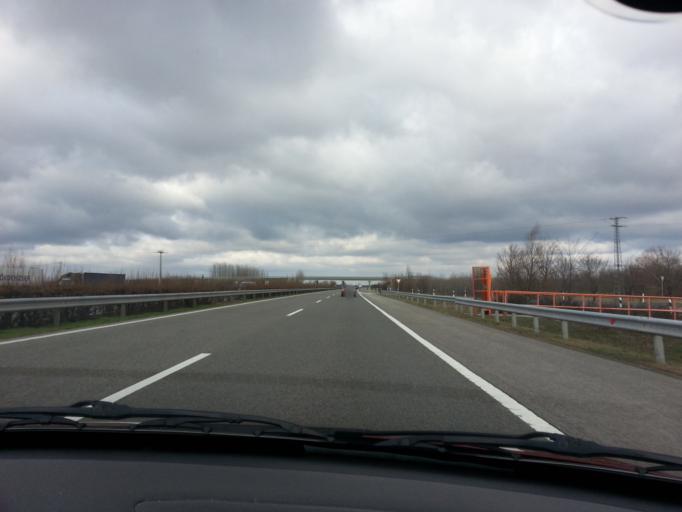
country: HU
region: Csongrad
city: Csengele
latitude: 46.5451
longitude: 19.8852
